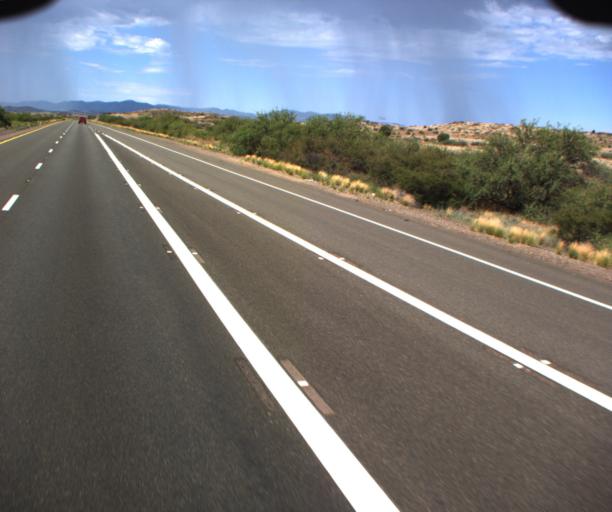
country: US
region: Arizona
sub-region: Yavapai County
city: Cordes Lakes
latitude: 34.4009
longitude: -112.0759
